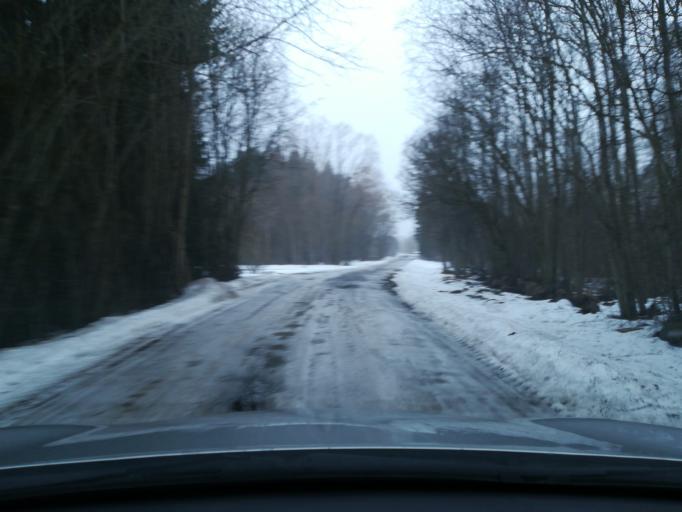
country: EE
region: Harju
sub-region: Rae vald
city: Jueri
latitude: 59.3779
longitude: 24.8835
